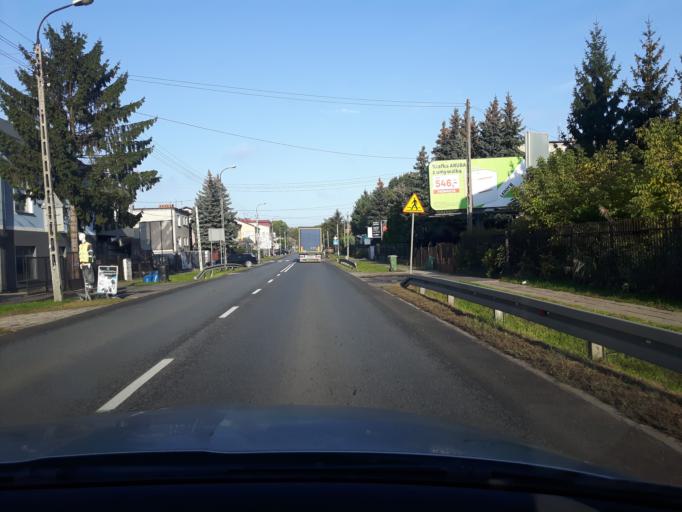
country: PL
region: Masovian Voivodeship
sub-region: Warszawa
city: Targowek
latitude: 52.2884
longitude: 21.0732
